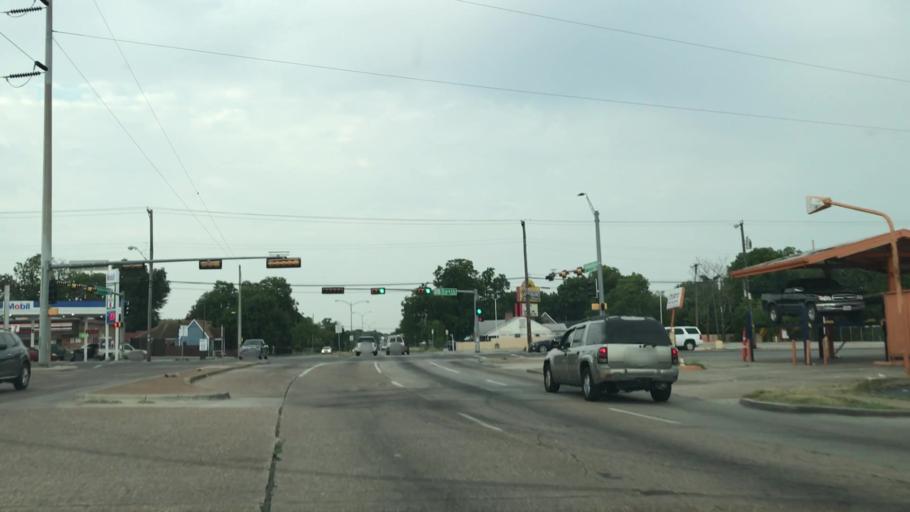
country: US
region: Texas
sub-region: Dallas County
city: Cockrell Hill
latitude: 32.7500
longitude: -96.8741
